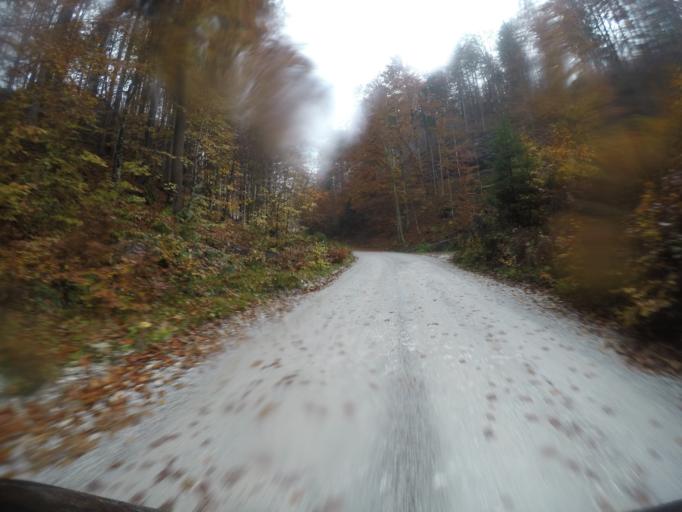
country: SI
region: Kranjska Gora
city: Mojstrana
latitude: 46.4340
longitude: 13.8873
